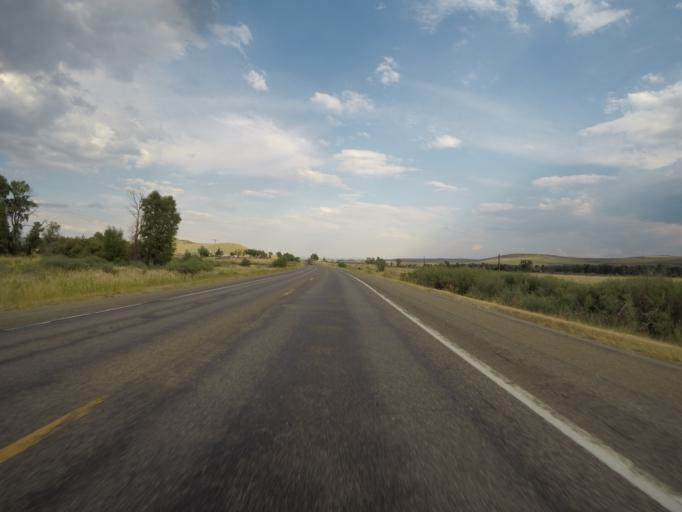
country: US
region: Colorado
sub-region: Moffat County
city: Craig
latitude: 40.5295
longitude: -107.4341
